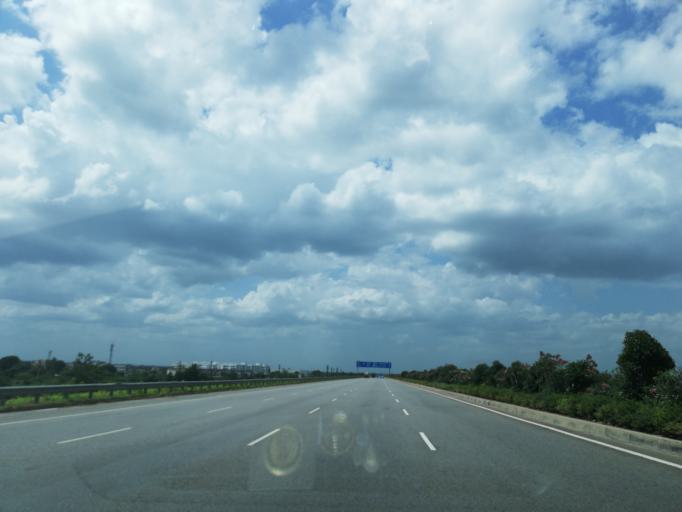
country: IN
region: Telangana
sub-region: Medak
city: Serilingampalle
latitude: 17.4404
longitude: 78.2589
